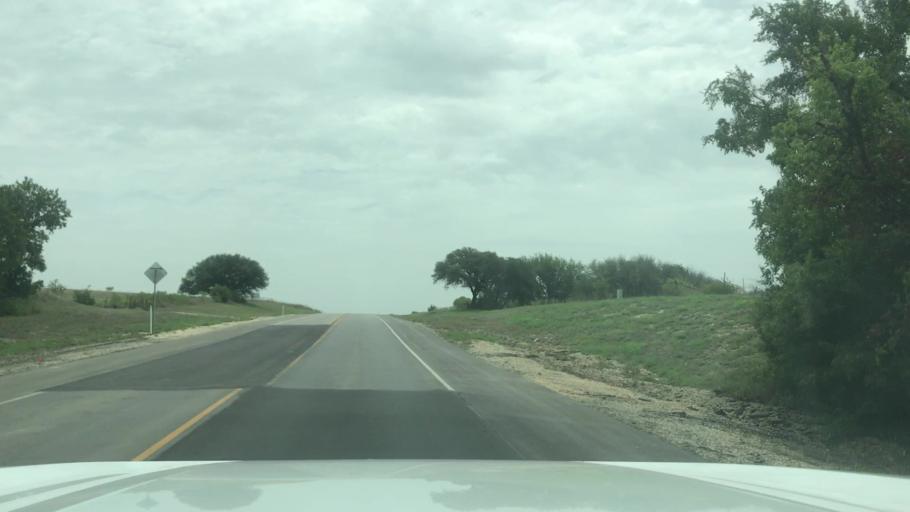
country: US
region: Texas
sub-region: Erath County
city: Dublin
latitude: 32.0735
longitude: -98.2272
